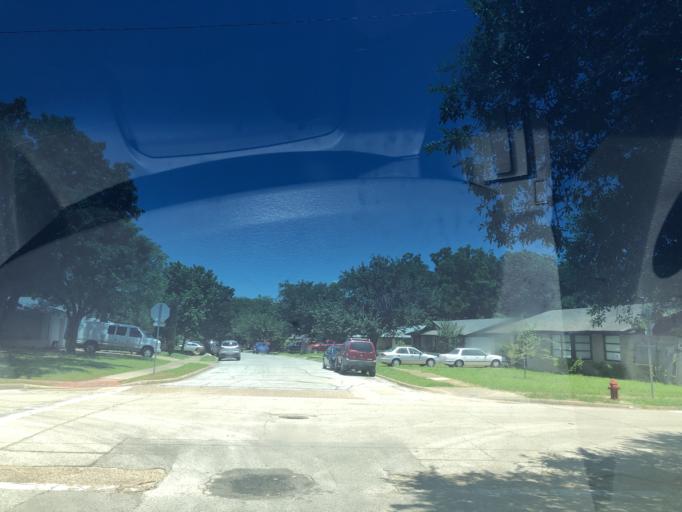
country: US
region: Texas
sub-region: Dallas County
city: Grand Prairie
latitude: 32.7174
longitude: -97.0112
